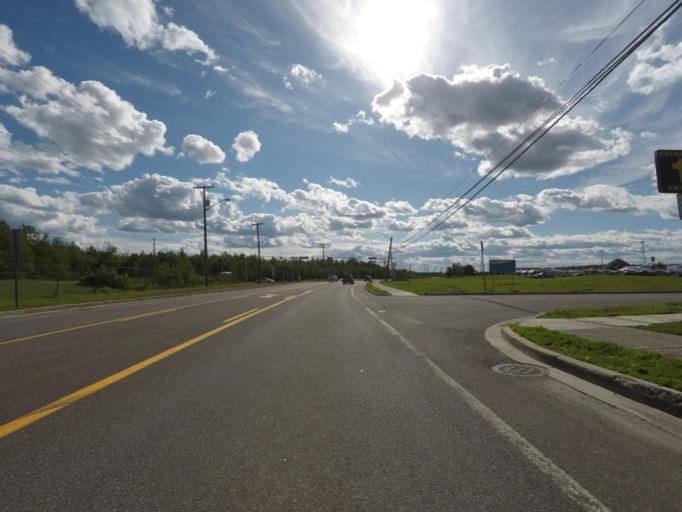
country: CA
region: New Brunswick
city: Moncton
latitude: 46.0943
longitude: -64.8294
